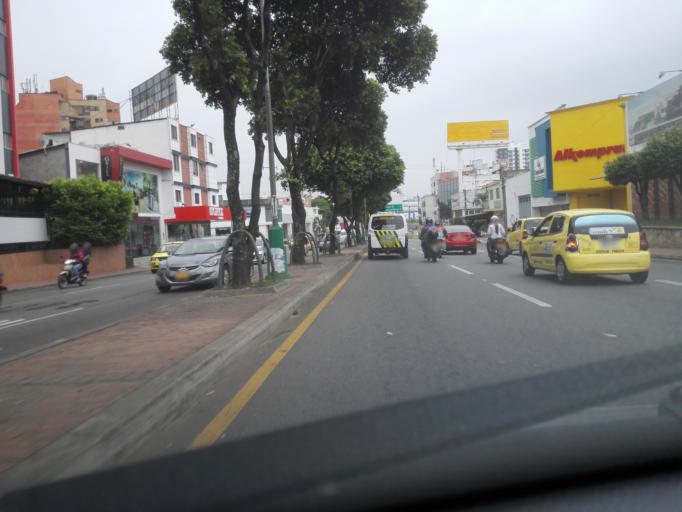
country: CO
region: Santander
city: Bucaramanga
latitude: 7.1110
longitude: -73.1145
